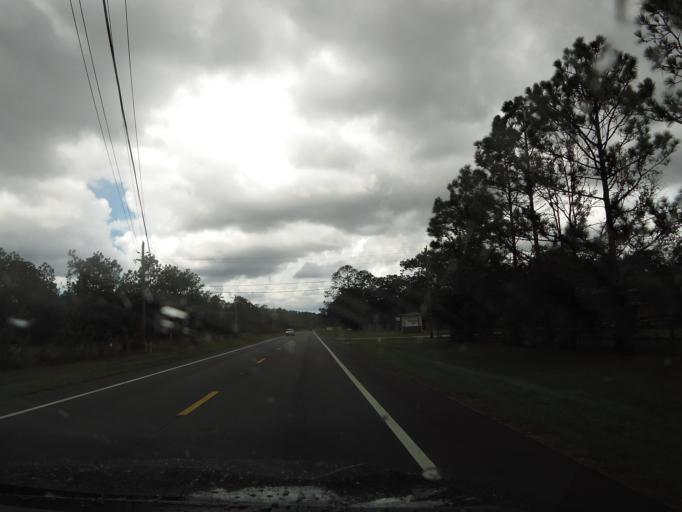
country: US
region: Florida
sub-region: Clay County
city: Asbury Lake
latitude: 30.0324
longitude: -81.8188
